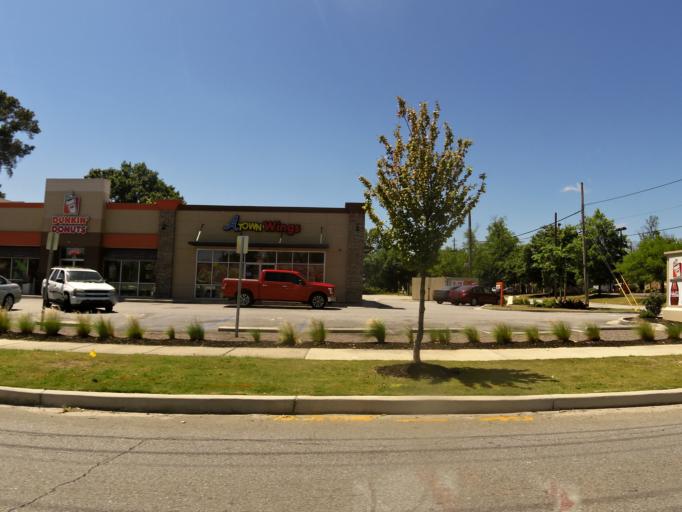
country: US
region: Georgia
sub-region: Richmond County
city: Augusta
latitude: 33.4755
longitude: -81.9950
